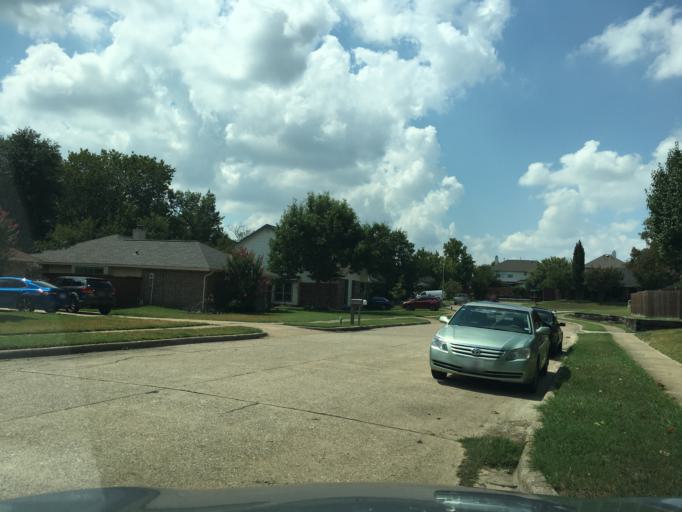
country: US
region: Texas
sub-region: Dallas County
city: Garland
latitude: 32.9504
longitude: -96.6352
